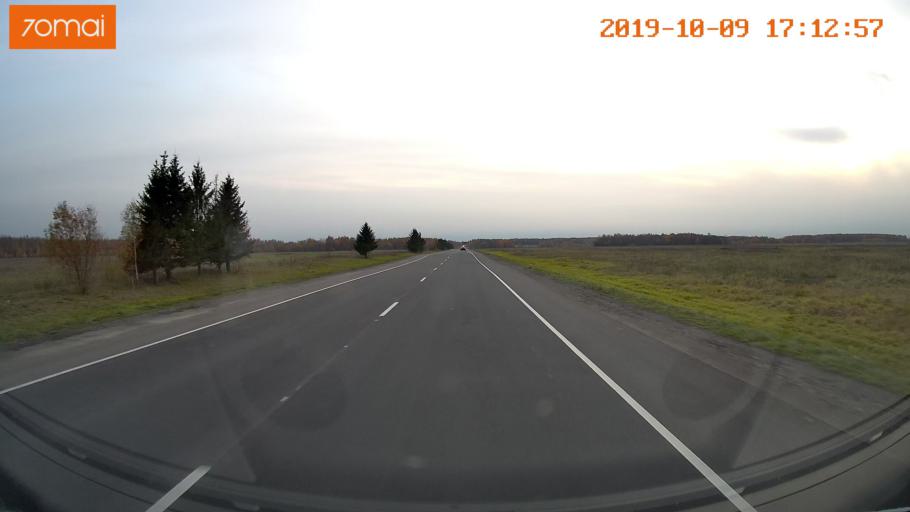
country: RU
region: Ivanovo
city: Privolzhsk
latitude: 57.3215
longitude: 41.2326
